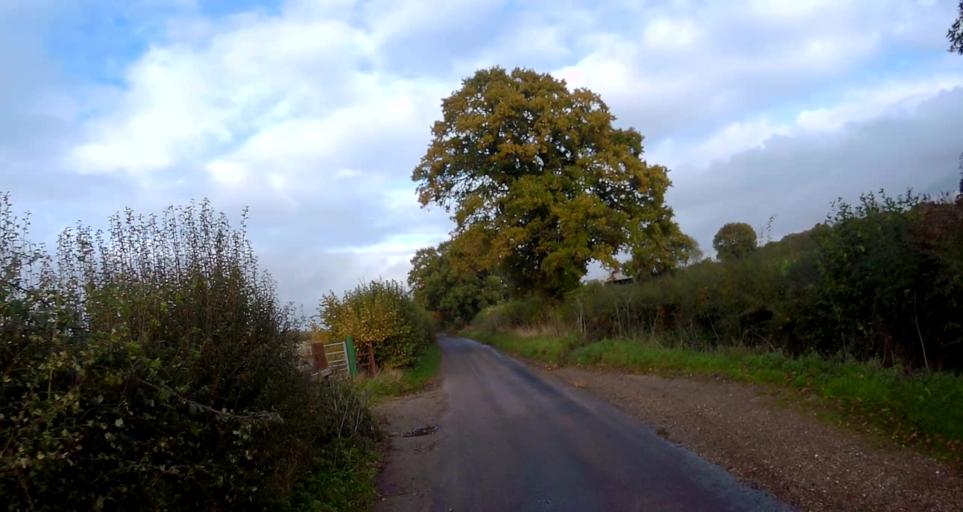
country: GB
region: England
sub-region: Hampshire
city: Four Marks
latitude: 51.1386
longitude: -1.1016
